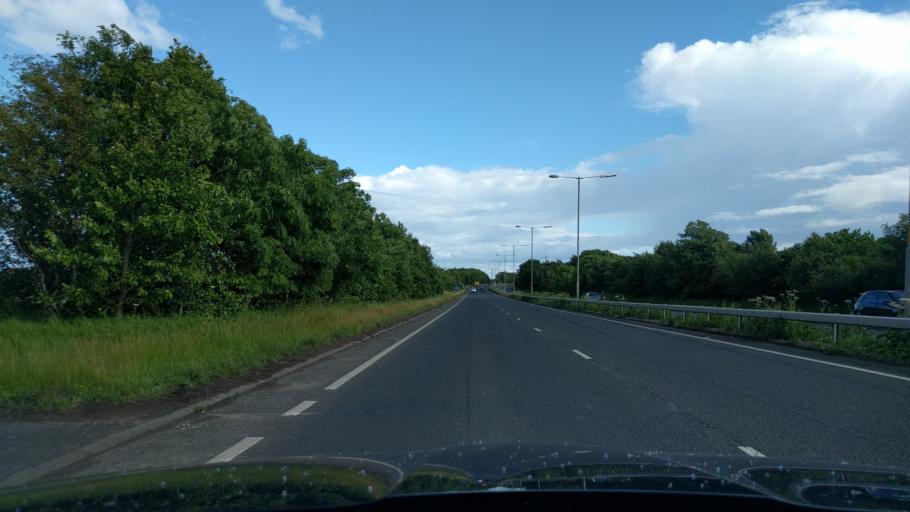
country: GB
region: England
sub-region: Northumberland
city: Newbiggin-by-the-Sea
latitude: 55.1826
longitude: -1.5359
